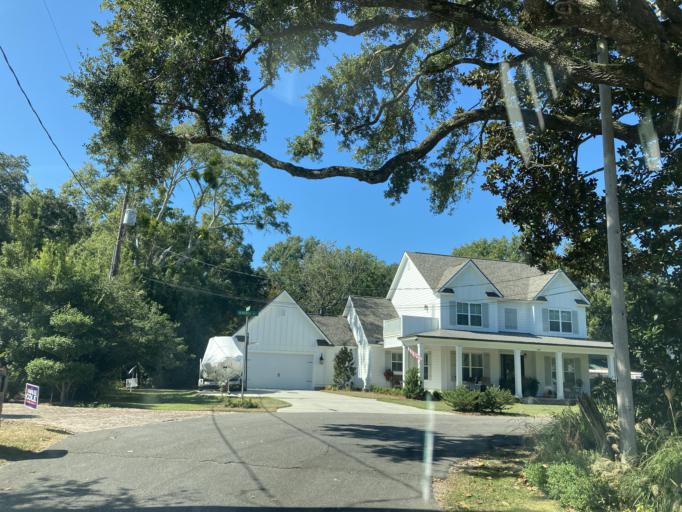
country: US
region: Mississippi
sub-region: Jackson County
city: Ocean Springs
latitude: 30.4094
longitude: -88.8362
